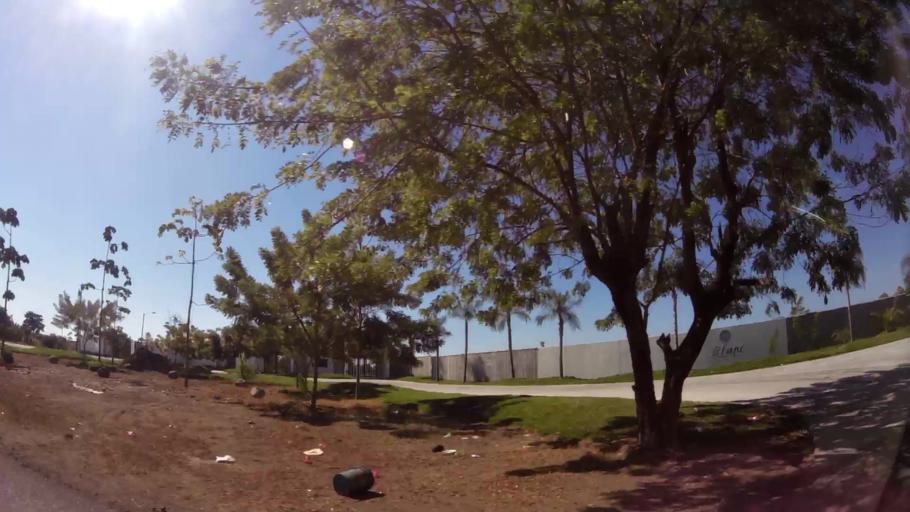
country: GT
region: Escuintla
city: Iztapa
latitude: 13.9200
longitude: -90.5637
